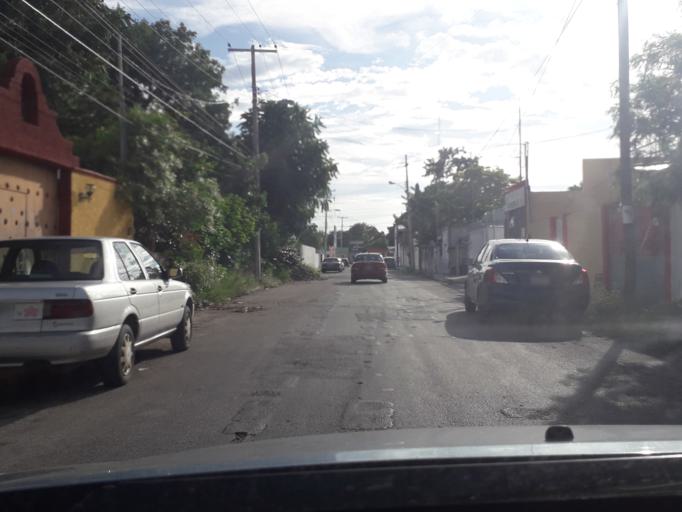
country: MX
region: Yucatan
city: Merida
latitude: 21.0033
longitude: -89.6381
